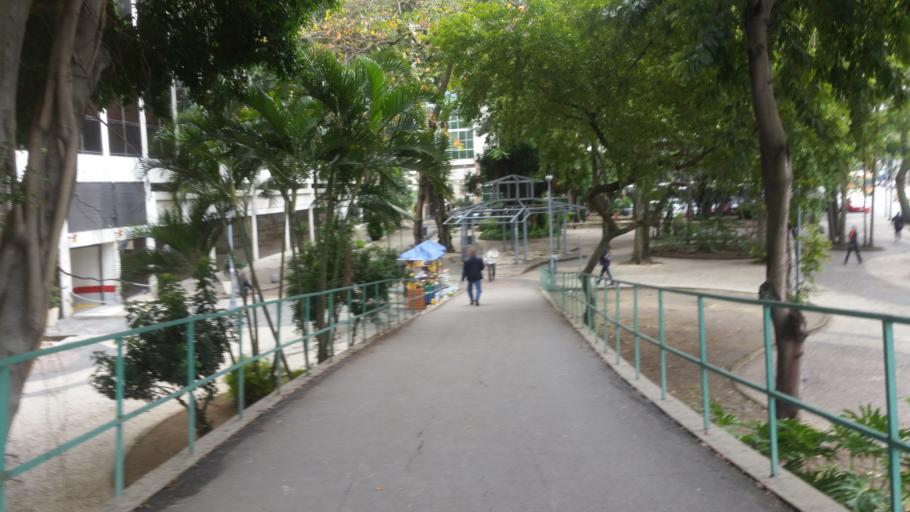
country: BR
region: Rio de Janeiro
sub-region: Rio De Janeiro
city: Rio de Janeiro
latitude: -22.9101
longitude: -43.1686
